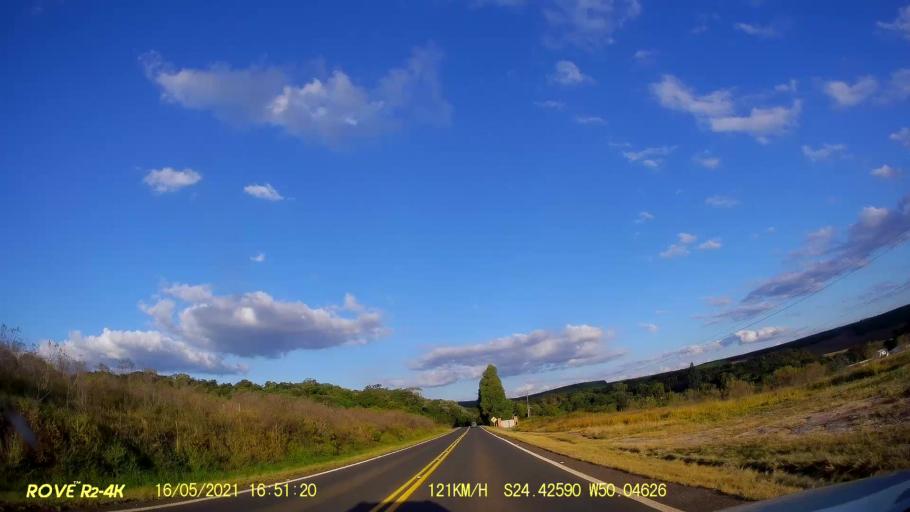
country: BR
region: Parana
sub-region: Pirai Do Sul
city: Pirai do Sul
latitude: -24.4260
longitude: -50.0461
